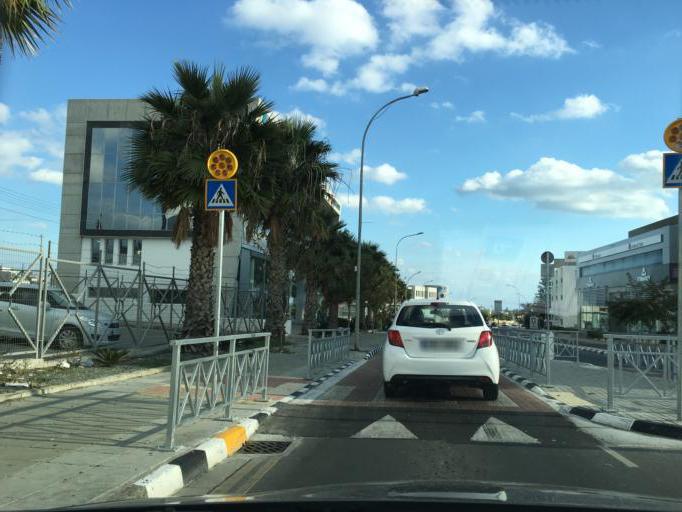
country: CY
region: Limassol
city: Limassol
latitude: 34.6986
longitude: 33.0629
